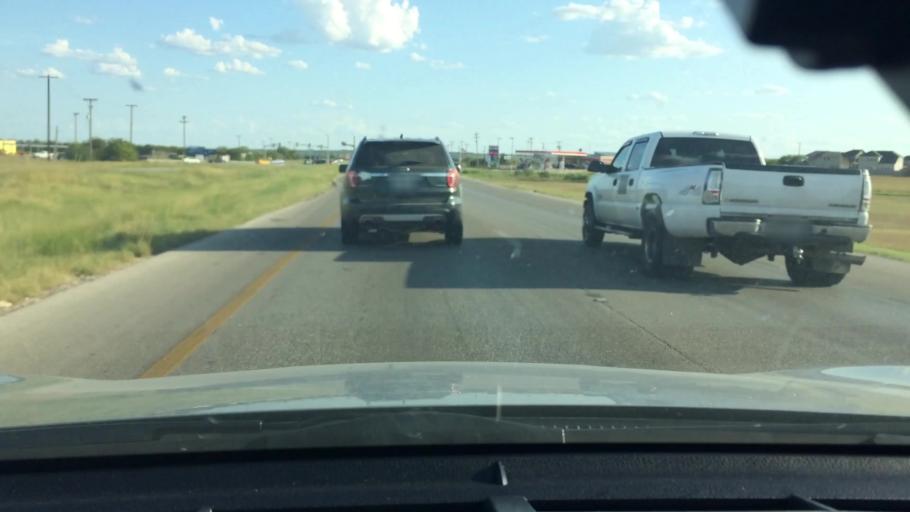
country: US
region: Texas
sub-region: Bexar County
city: Converse
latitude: 29.5066
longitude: -98.2874
